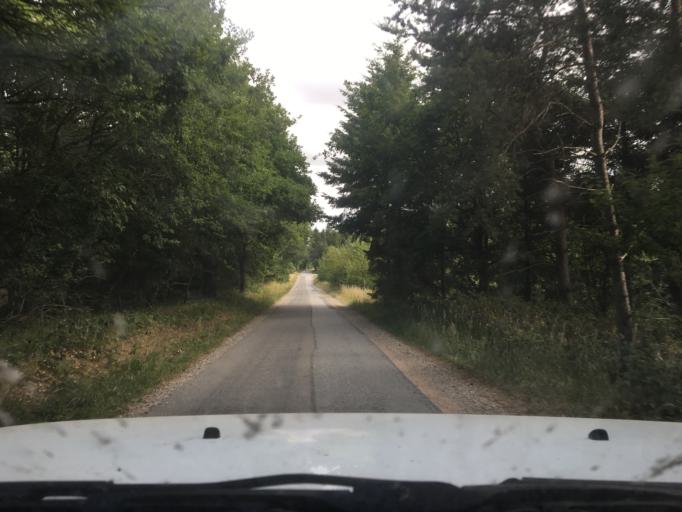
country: DK
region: Central Jutland
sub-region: Syddjurs Kommune
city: Ryomgard
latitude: 56.4745
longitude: 10.6186
